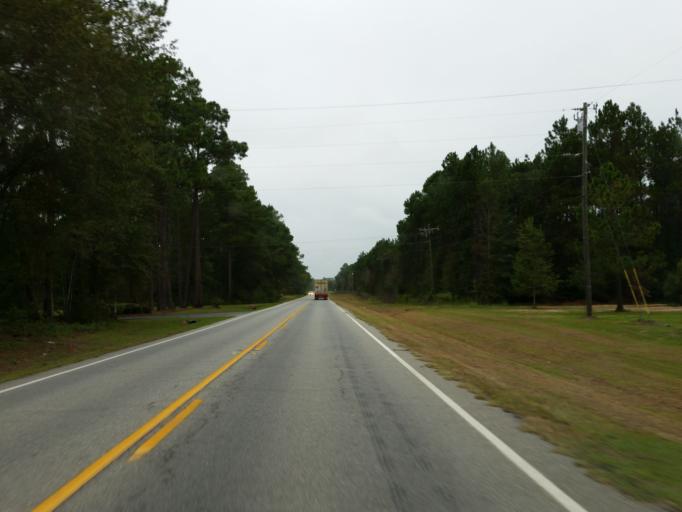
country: US
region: Georgia
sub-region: Berrien County
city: Ray City
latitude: 31.0777
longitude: -83.2199
